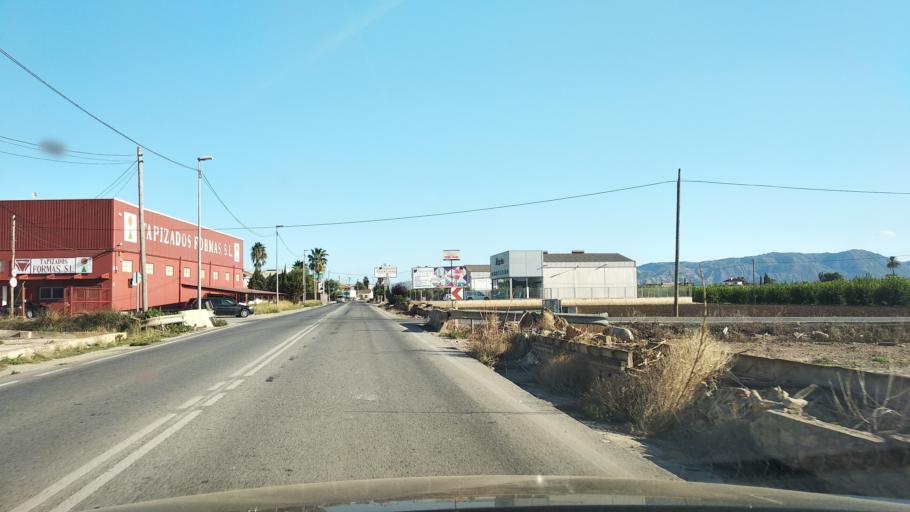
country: ES
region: Murcia
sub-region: Murcia
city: Santomera
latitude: 38.0435
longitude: -1.0515
